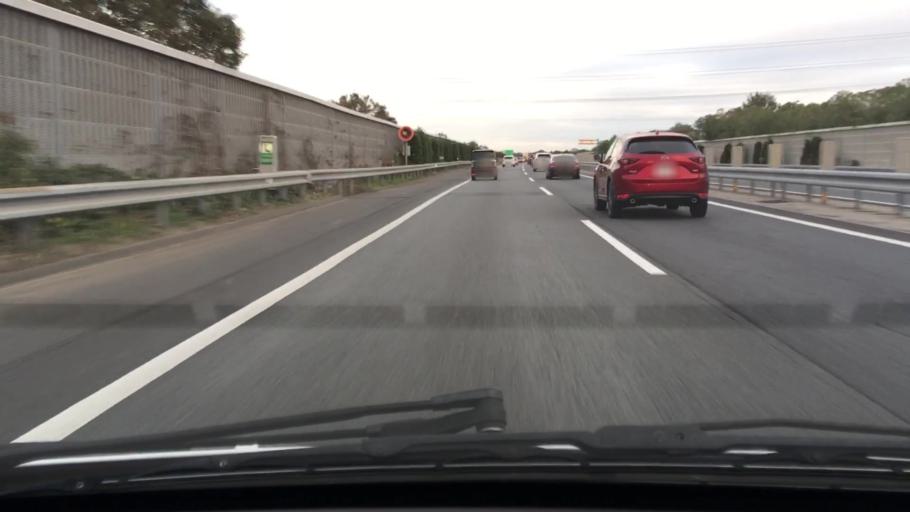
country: JP
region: Chiba
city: Ichihara
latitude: 35.5075
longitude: 140.1067
